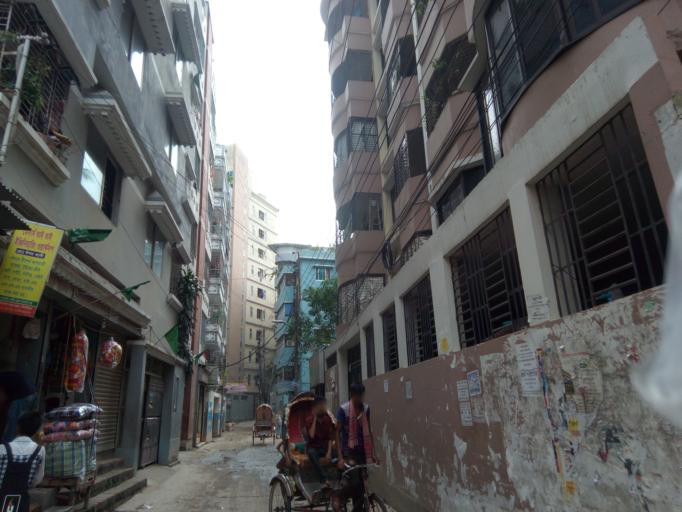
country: BD
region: Dhaka
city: Azimpur
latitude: 23.7425
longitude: 90.3696
